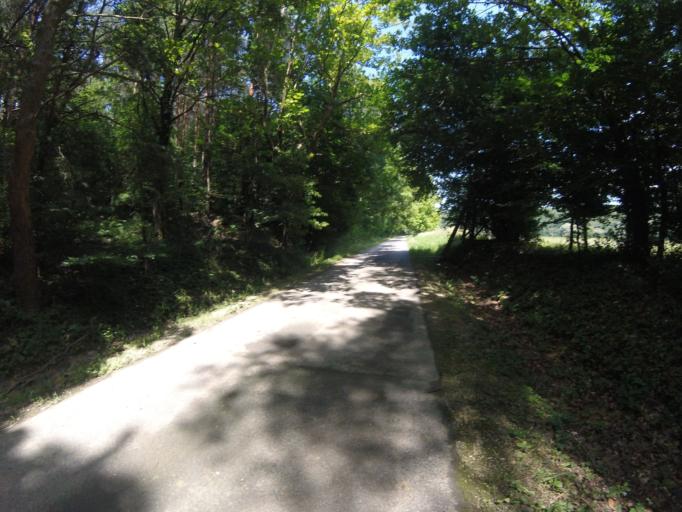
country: HU
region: Zala
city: Lenti
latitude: 46.5475
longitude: 16.6105
